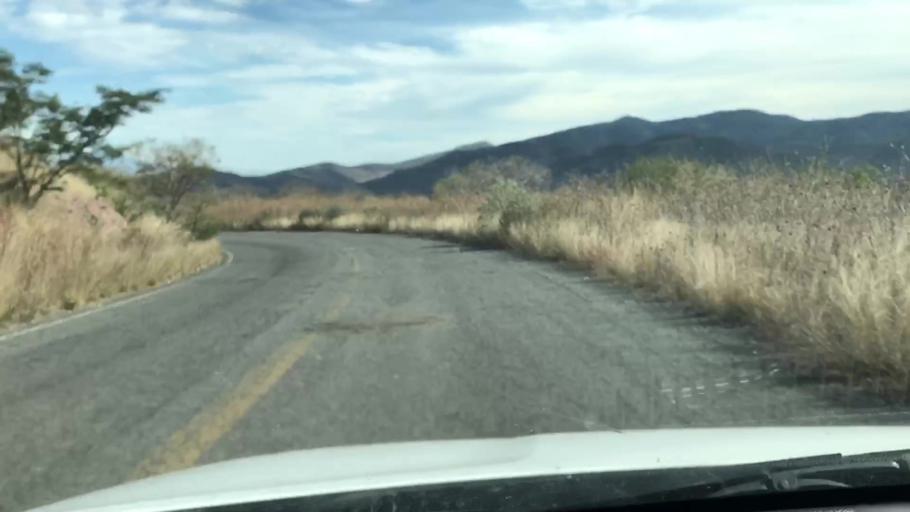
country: MX
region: Jalisco
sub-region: Zacoalco de Torres
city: Barranca de Otates (Barranca de Otatan)
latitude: 20.2446
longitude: -103.6696
